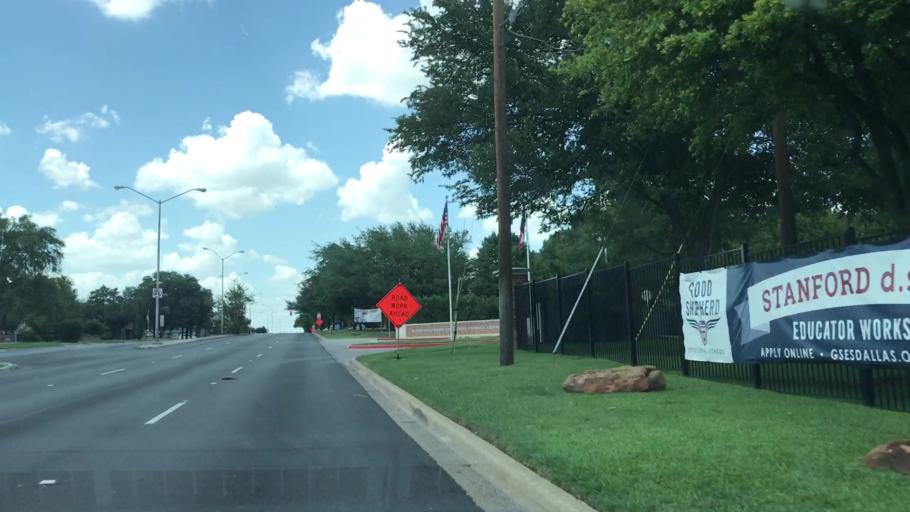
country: US
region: Texas
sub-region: Dallas County
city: Addison
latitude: 32.9002
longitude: -96.8382
